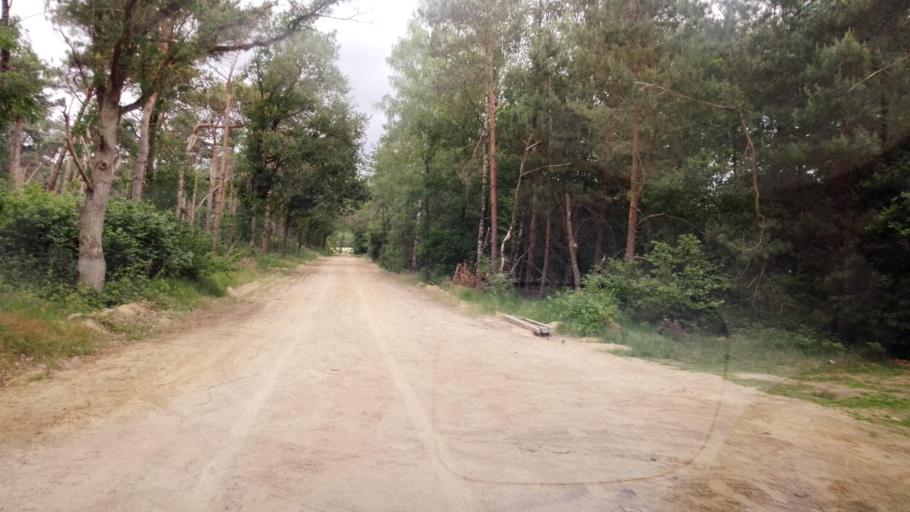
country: NL
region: Limburg
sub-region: Gemeente Venlo
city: Tegelen
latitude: 51.3998
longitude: 6.1071
